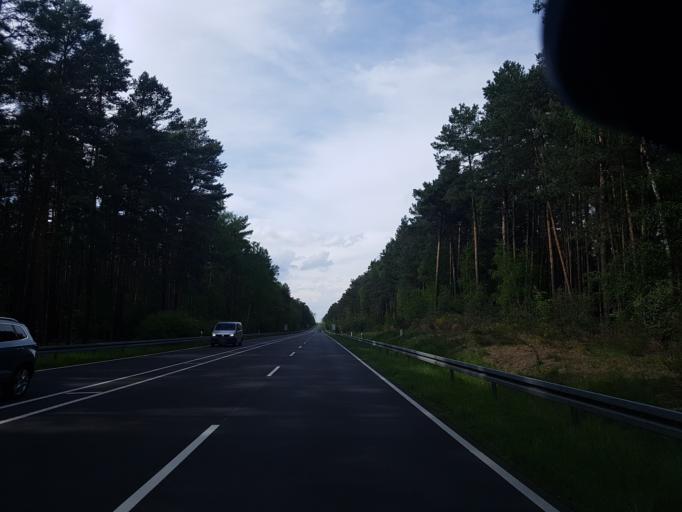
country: DE
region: Saxony
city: Gross Duben
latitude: 51.6559
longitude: 14.5330
